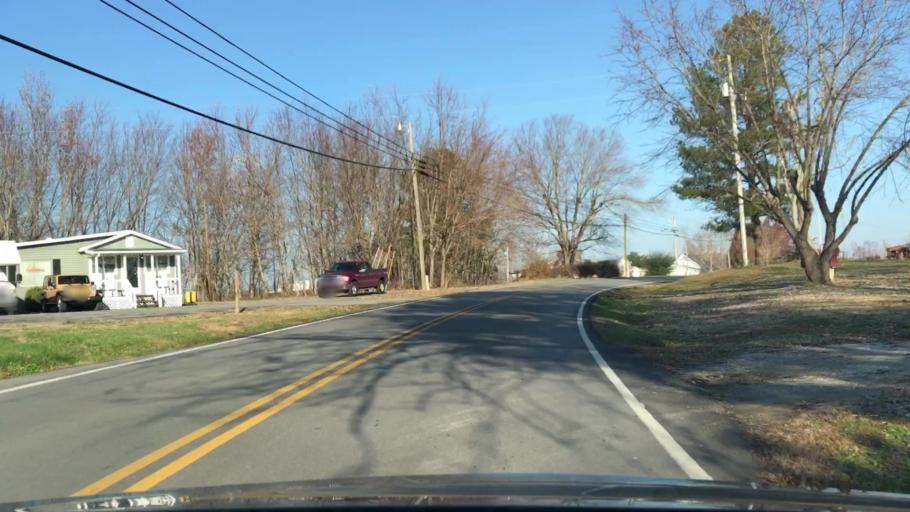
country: US
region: Kentucky
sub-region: Edmonson County
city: Brownsville
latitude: 37.2899
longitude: -86.2854
